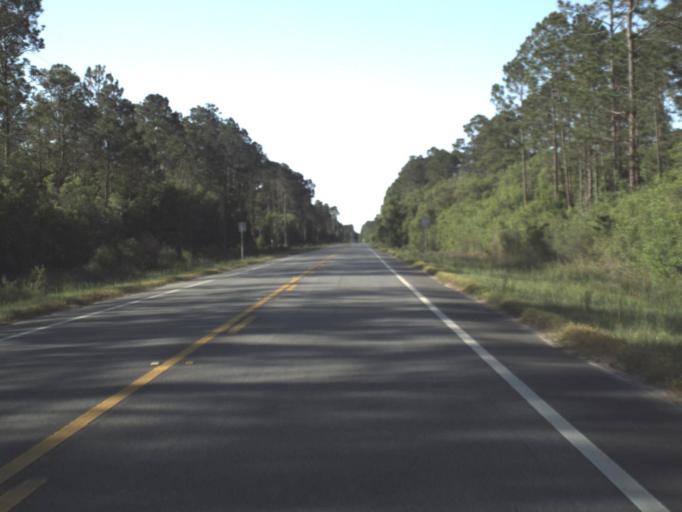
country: US
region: Florida
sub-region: Liberty County
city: Bristol
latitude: 30.3377
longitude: -84.8221
